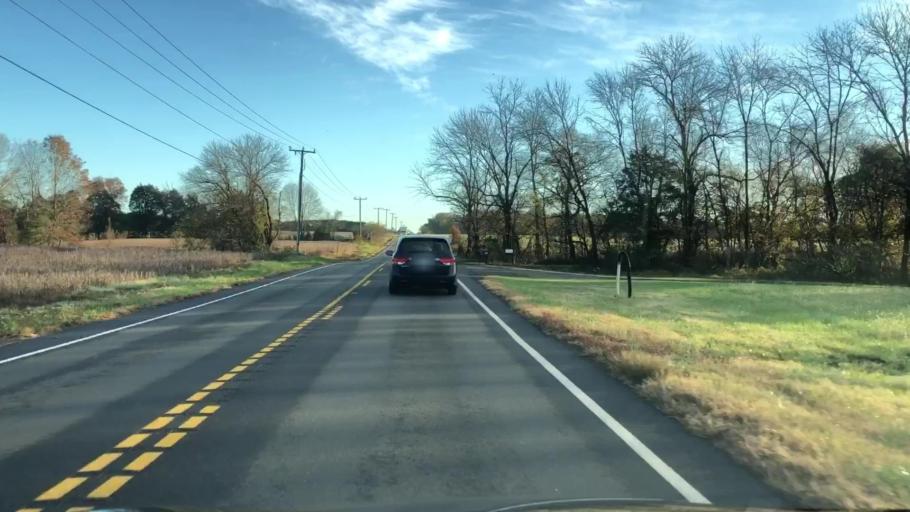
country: US
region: Virginia
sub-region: Fauquier County
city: Bealeton
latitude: 38.6126
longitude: -77.7082
